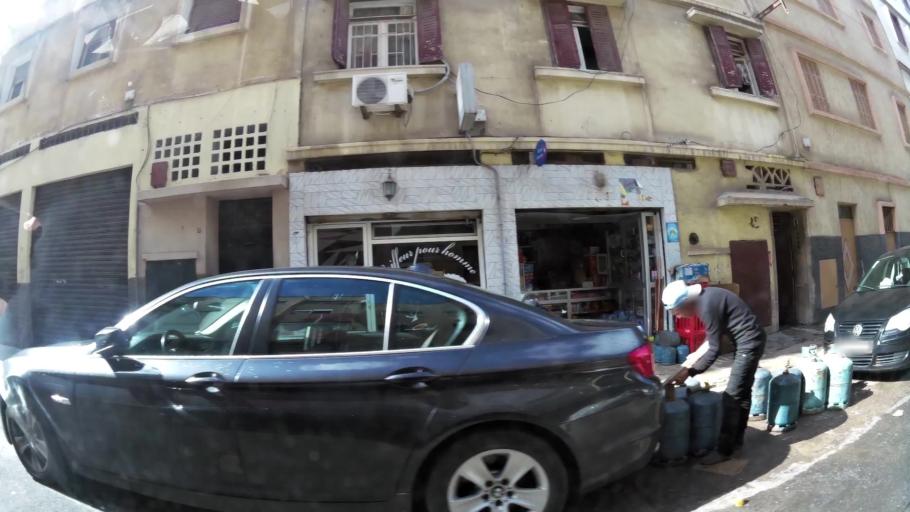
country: MA
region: Grand Casablanca
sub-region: Casablanca
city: Casablanca
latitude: 33.5733
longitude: -7.6267
